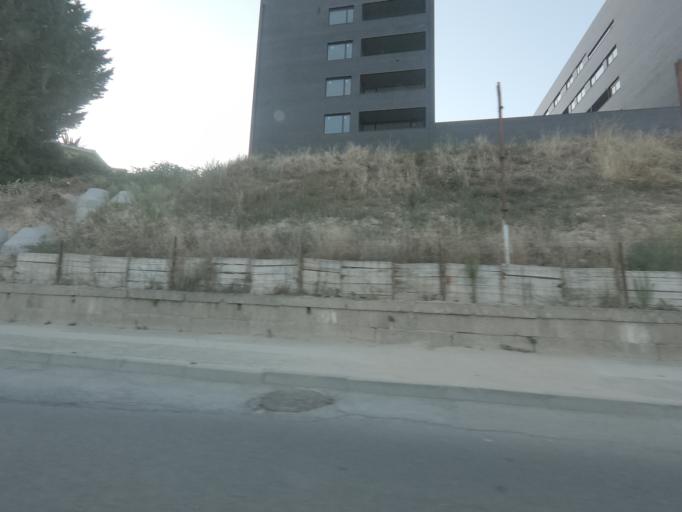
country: PT
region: Vila Real
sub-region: Vila Real
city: Vila Real
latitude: 41.3068
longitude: -7.7390
